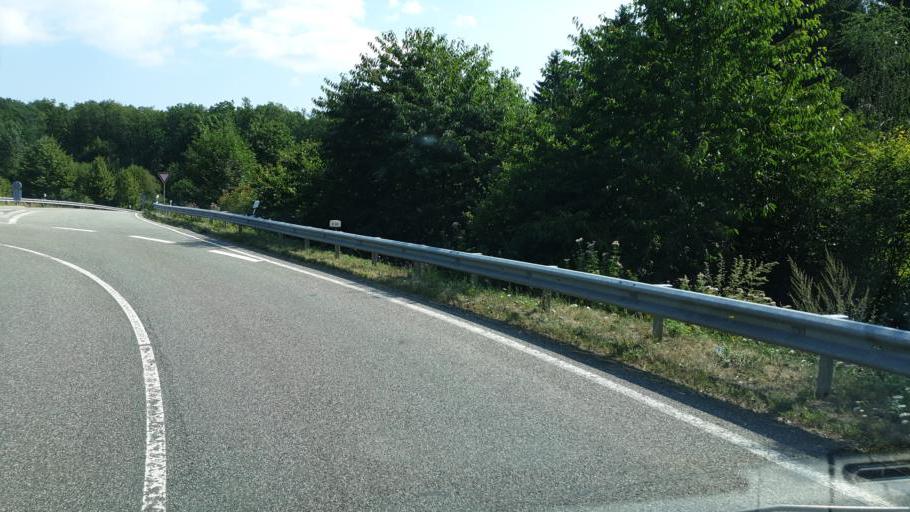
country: DE
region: Rheinland-Pfalz
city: Neuhausel
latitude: 50.3909
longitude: 7.7206
